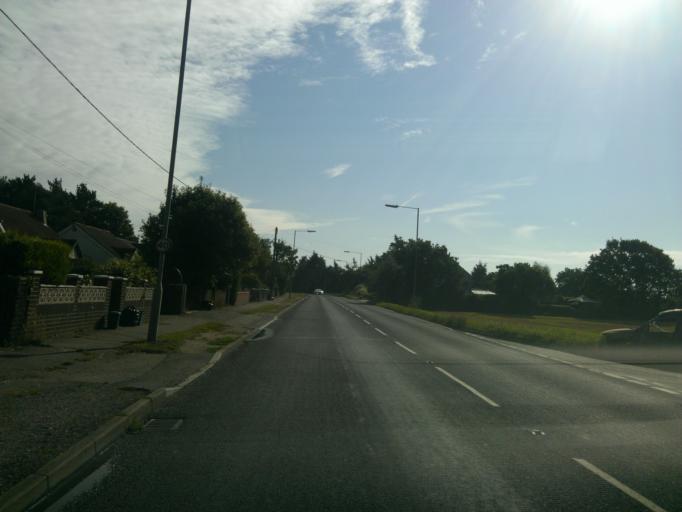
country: GB
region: England
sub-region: Essex
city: Saint Osyth
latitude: 51.8003
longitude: 1.1107
